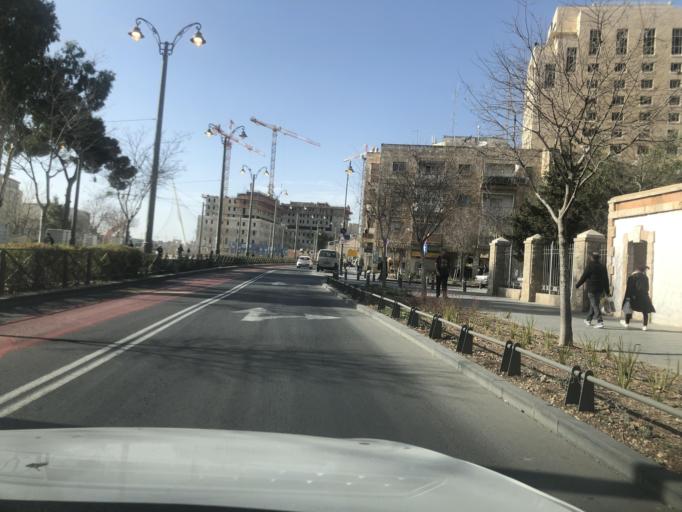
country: IL
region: Jerusalem
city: West Jerusalem
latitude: 31.7871
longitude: 35.2089
